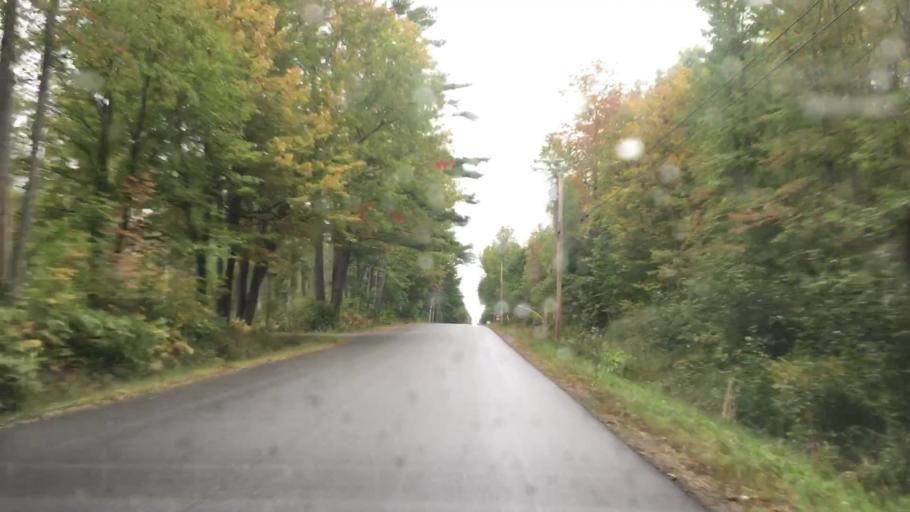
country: US
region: Maine
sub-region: Cumberland County
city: Harrison
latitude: 44.0931
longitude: -70.6560
